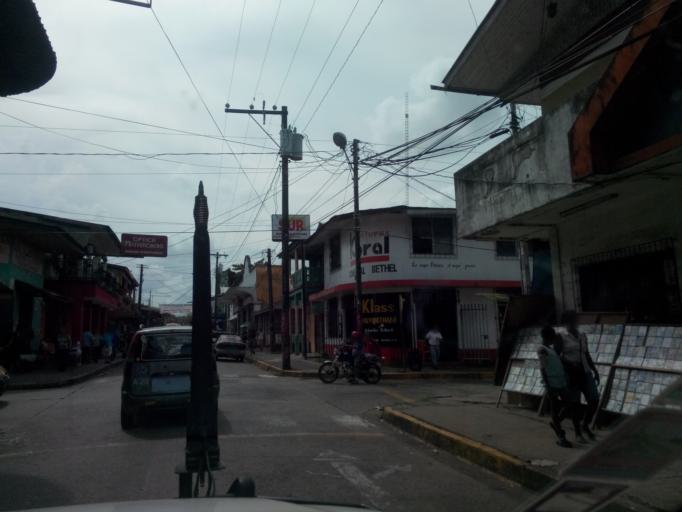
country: NI
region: Atlantico Sur
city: Bluefields
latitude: 12.0120
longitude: -83.7616
